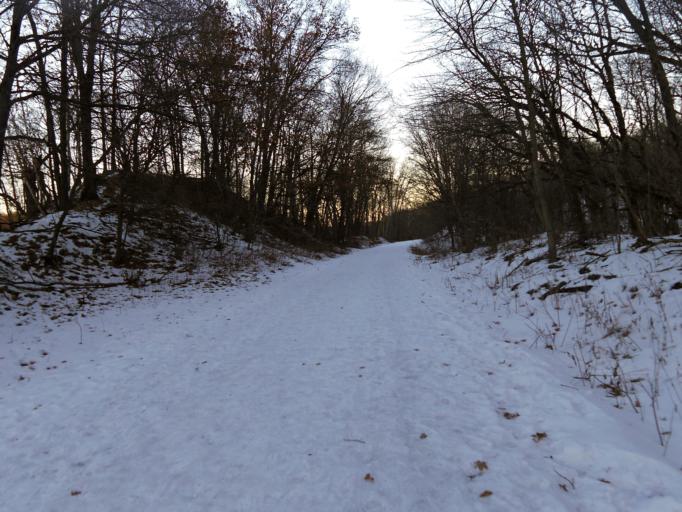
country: US
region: Minnesota
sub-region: Washington County
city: Stillwater
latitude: 45.0751
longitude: -92.8142
